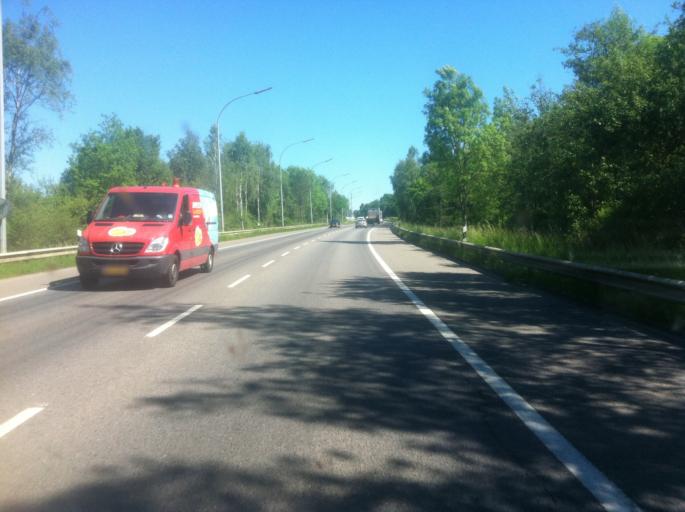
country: LU
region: Luxembourg
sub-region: Canton de Capellen
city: Garnich
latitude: 49.6386
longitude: 5.9549
